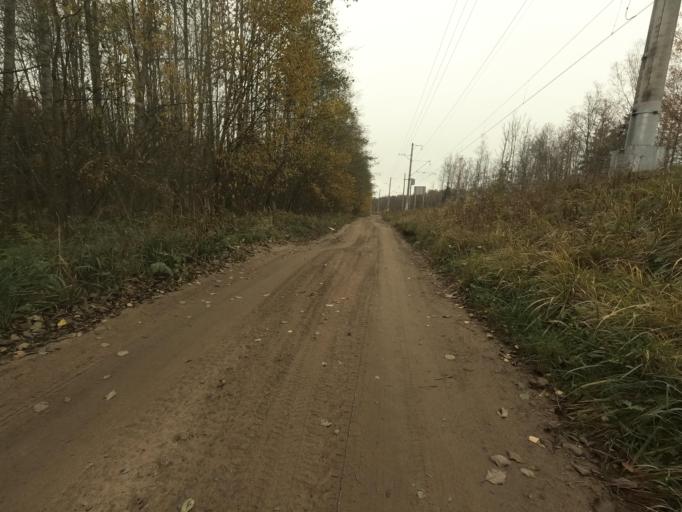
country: RU
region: Leningrad
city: Pavlovo
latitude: 59.7848
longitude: 30.8930
